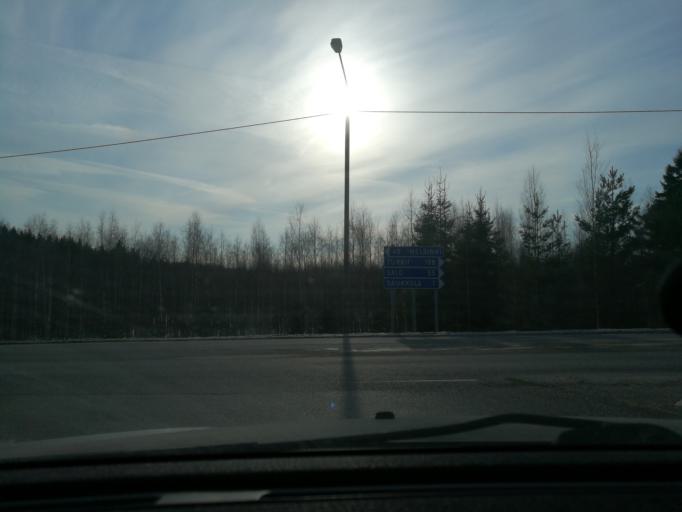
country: FI
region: Uusimaa
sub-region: Helsinki
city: Saukkola
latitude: 60.3841
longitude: 24.0842
